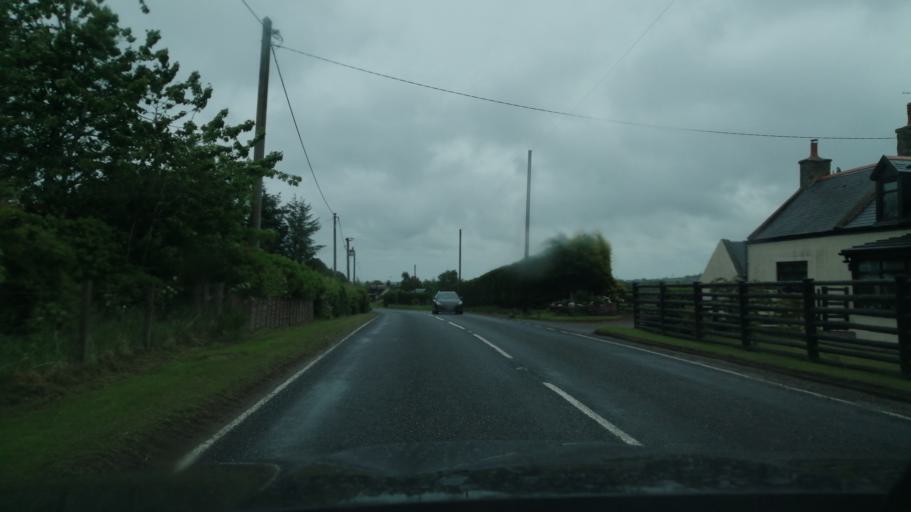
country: GB
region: Scotland
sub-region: Aberdeenshire
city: Portsoy
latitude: 57.5939
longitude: -2.7337
